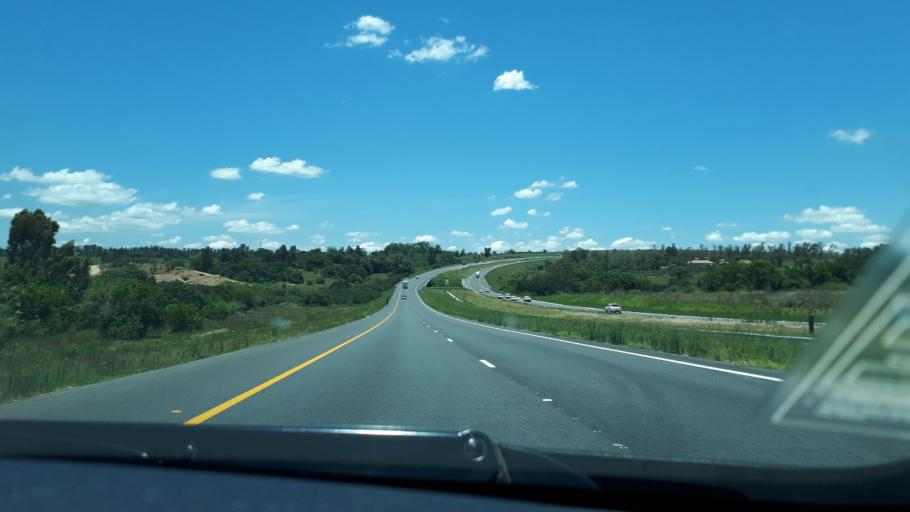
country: ZA
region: Gauteng
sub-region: City of Johannesburg Metropolitan Municipality
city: Diepsloot
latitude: -25.9519
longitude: 27.9552
